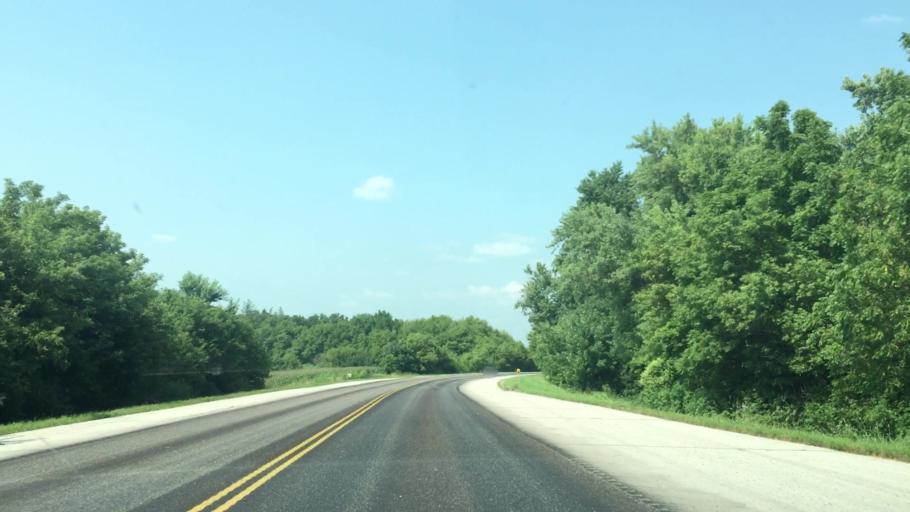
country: US
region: Minnesota
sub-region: Fillmore County
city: Harmony
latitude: 43.5061
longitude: -91.8712
